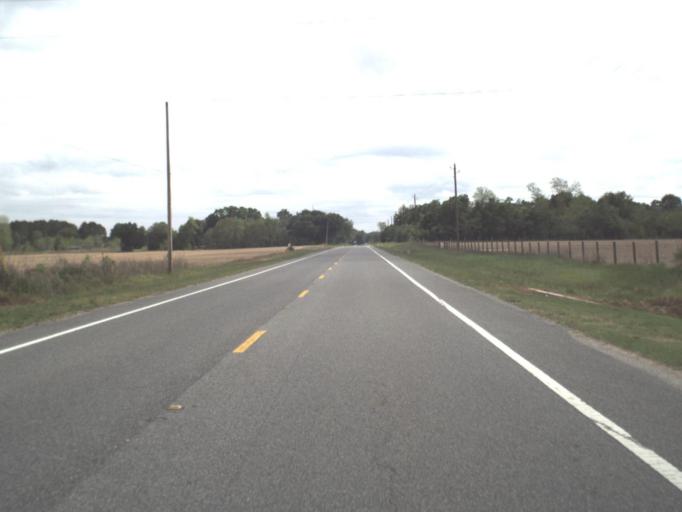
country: US
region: Florida
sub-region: Santa Rosa County
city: Point Baker
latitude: 30.7493
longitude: -87.0934
